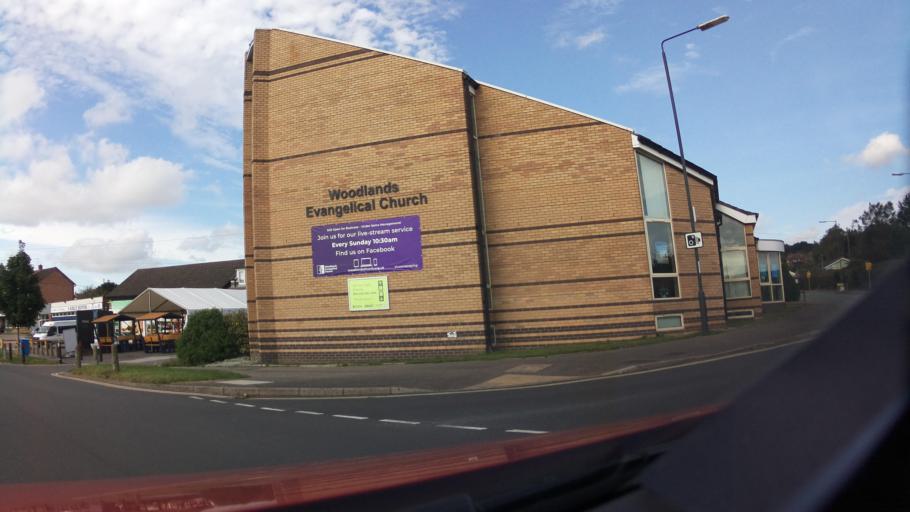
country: GB
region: England
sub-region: Derbyshire
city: Duffield
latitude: 52.9531
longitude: -1.4934
